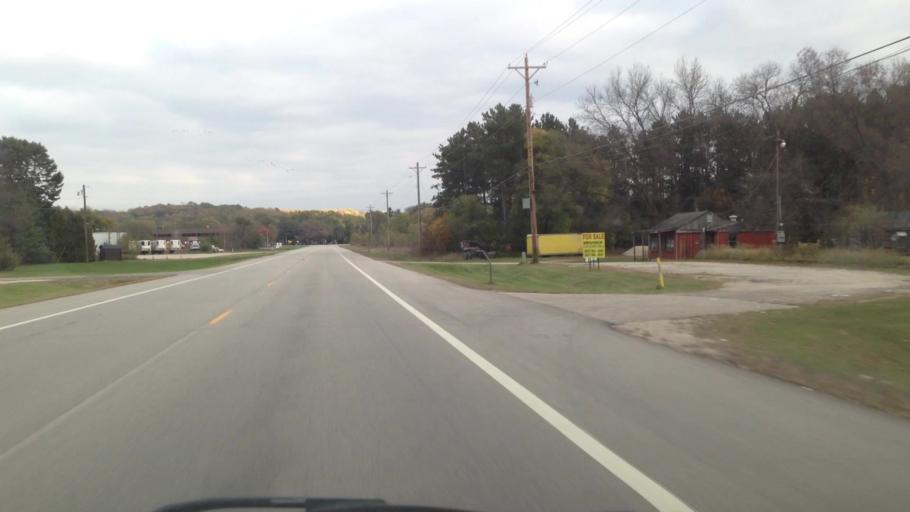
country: US
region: Minnesota
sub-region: Olmsted County
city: Rochester
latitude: 43.9874
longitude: -92.4100
